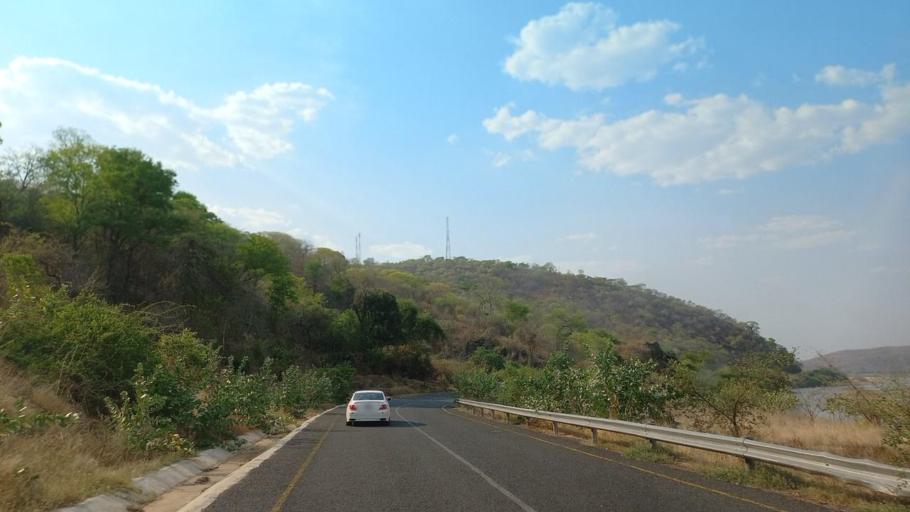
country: ZM
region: Lusaka
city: Luangwa
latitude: -15.0096
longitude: 30.2163
